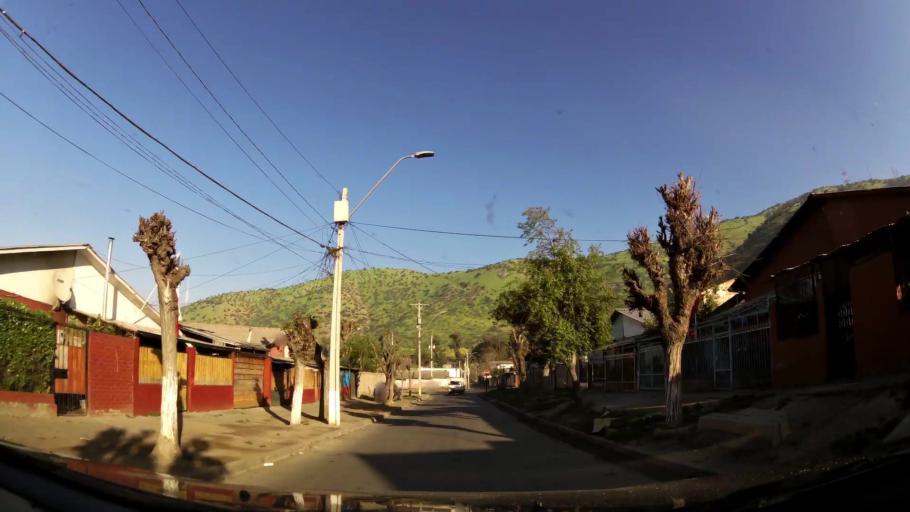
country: CL
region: Santiago Metropolitan
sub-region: Provincia de Chacabuco
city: Chicureo Abajo
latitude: -33.3613
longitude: -70.6307
